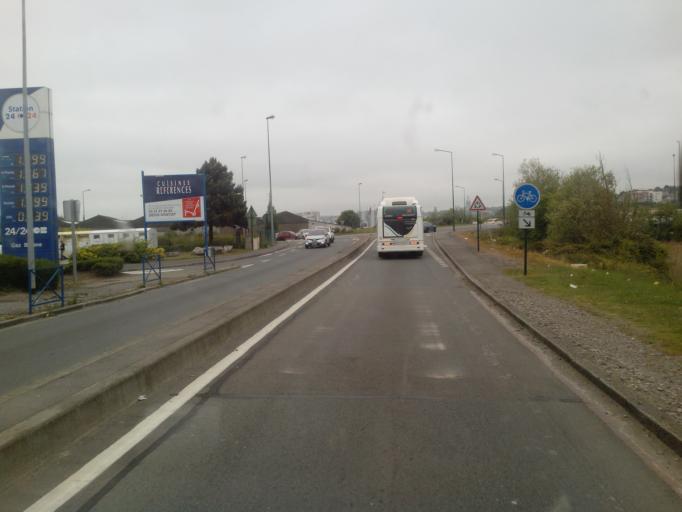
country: FR
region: Nord-Pas-de-Calais
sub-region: Departement du Pas-de-Calais
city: Boulogne-sur-Mer
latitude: 50.7017
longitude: 1.6091
